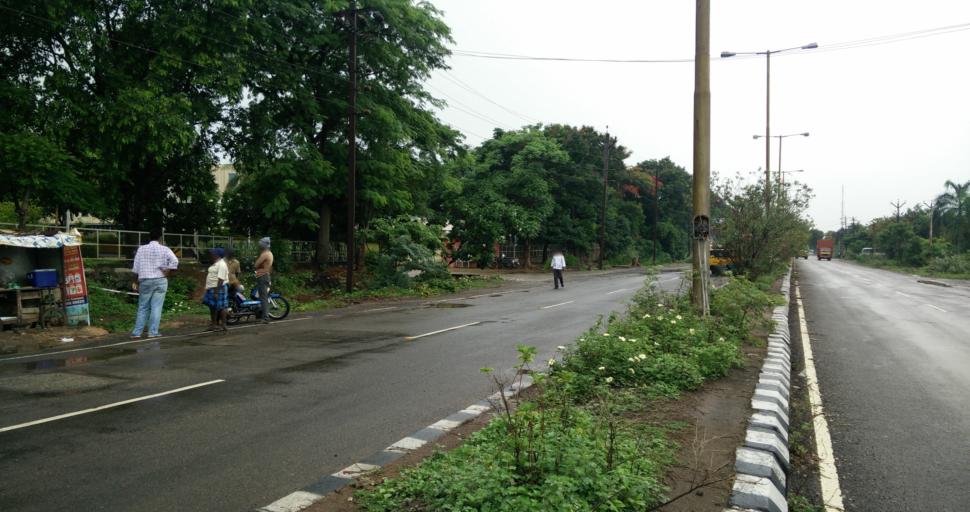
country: IN
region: Tamil Nadu
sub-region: Kancheepuram
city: Nandambakkam
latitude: 12.9995
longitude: 80.0205
